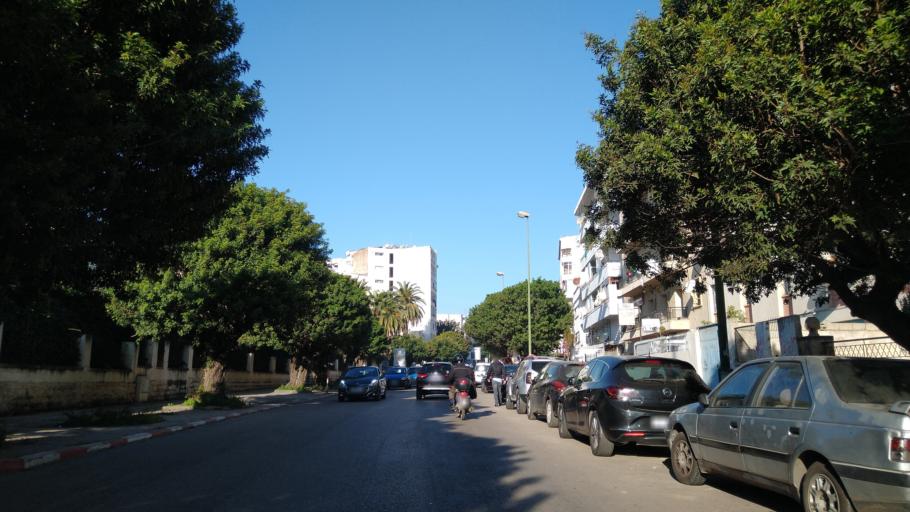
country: MA
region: Rabat-Sale-Zemmour-Zaer
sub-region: Rabat
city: Rabat
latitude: 34.0189
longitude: -6.8448
